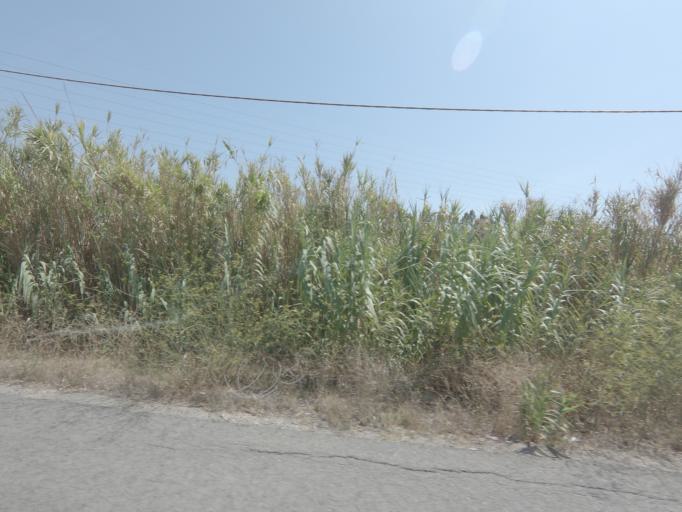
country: PT
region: Setubal
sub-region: Setubal
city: Setubal
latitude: 38.5307
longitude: -8.9200
